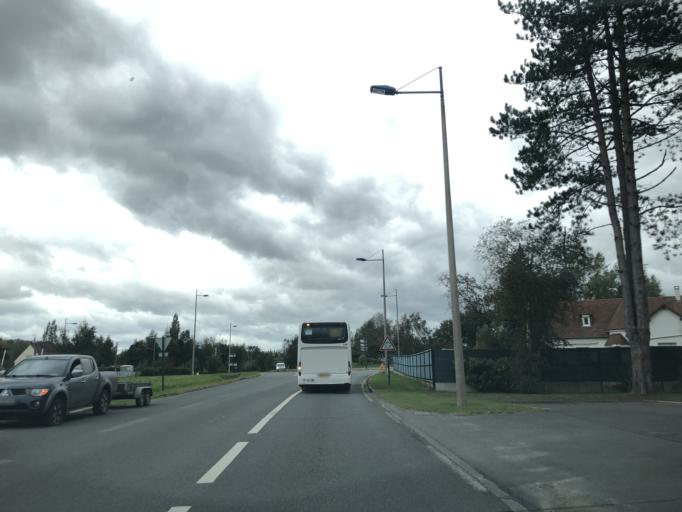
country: FR
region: Nord-Pas-de-Calais
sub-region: Departement du Pas-de-Calais
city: Saint-Josse
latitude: 50.4623
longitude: 1.6494
